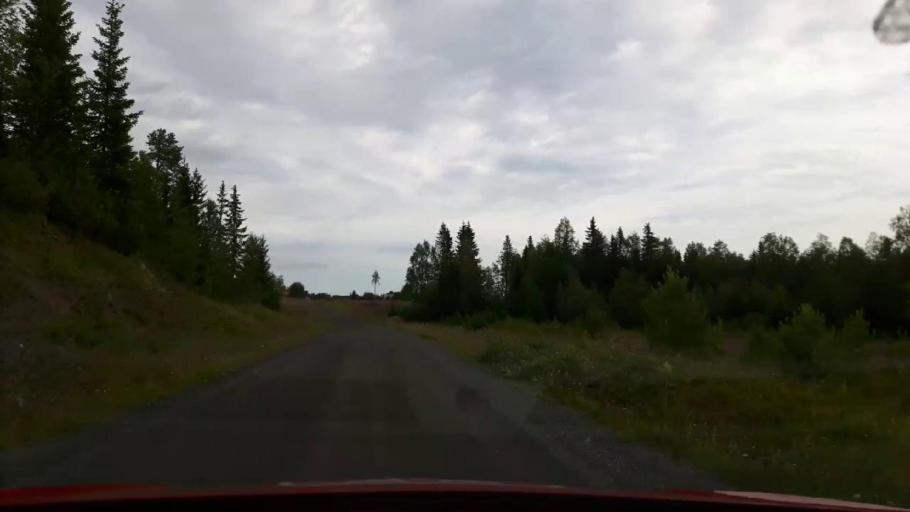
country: SE
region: Jaemtland
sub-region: OEstersunds Kommun
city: Lit
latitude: 63.4097
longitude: 15.2410
